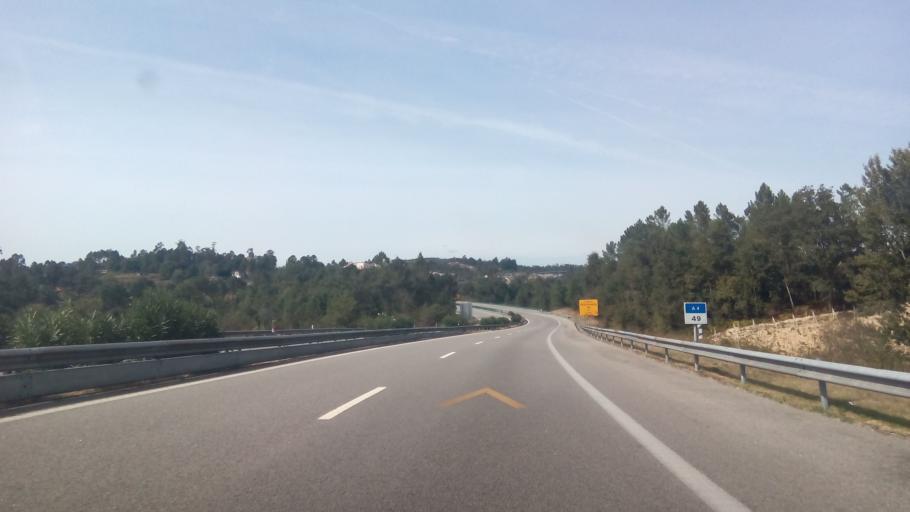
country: PT
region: Porto
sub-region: Marco de Canaveses
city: Marco de Canavezes
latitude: 41.2227
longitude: -8.1676
